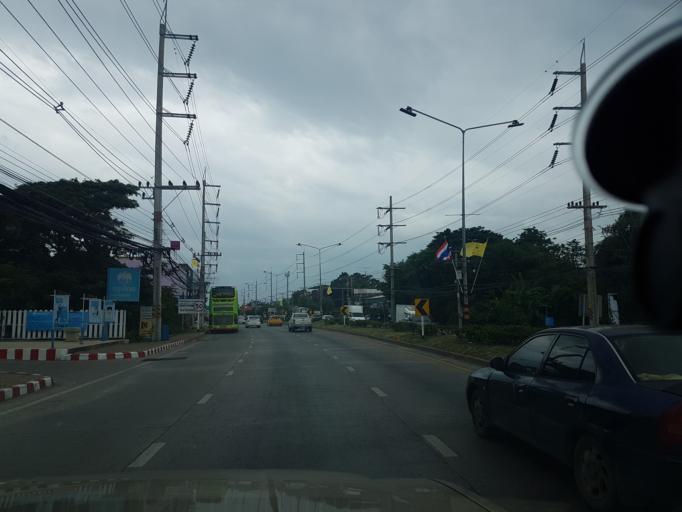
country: TH
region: Lop Buri
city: Lop Buri
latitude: 14.7993
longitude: 100.6602
